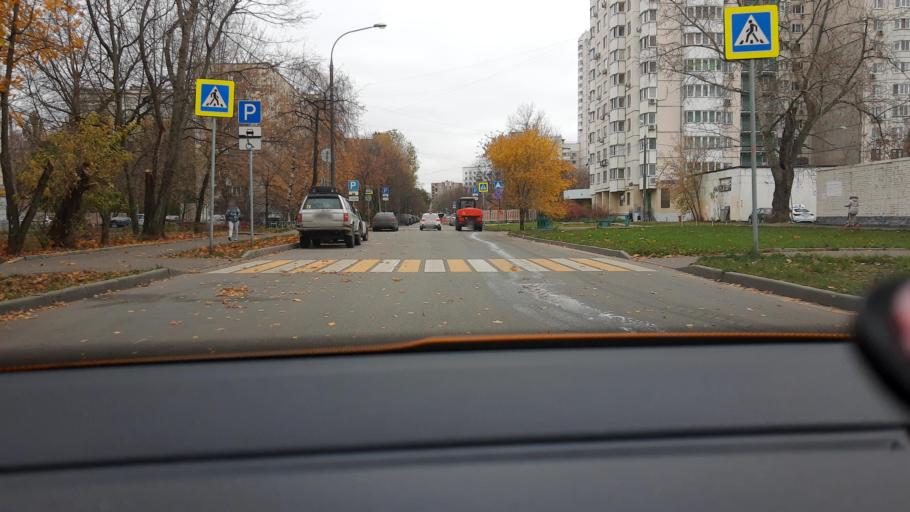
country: RU
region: Moscow
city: Perovo
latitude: 55.7498
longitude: 37.7912
